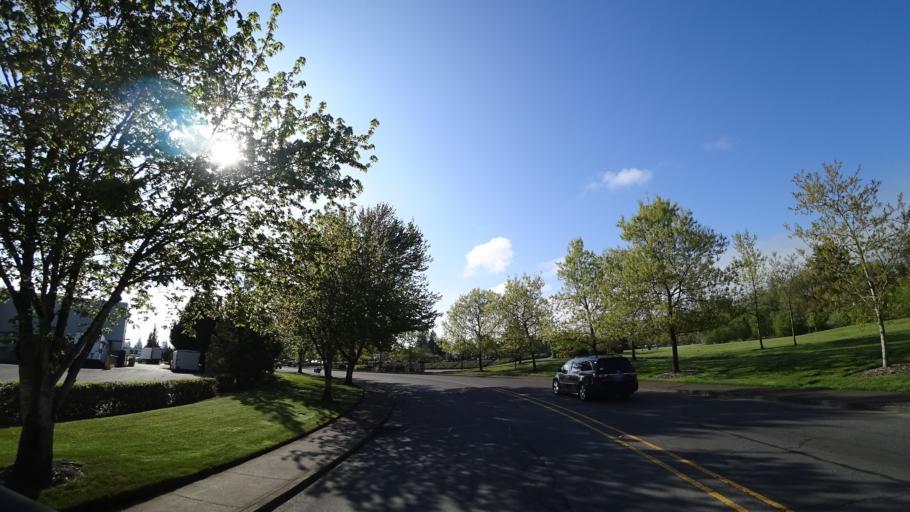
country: US
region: Oregon
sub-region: Washington County
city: Hillsboro
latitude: 45.5178
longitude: -123.0073
